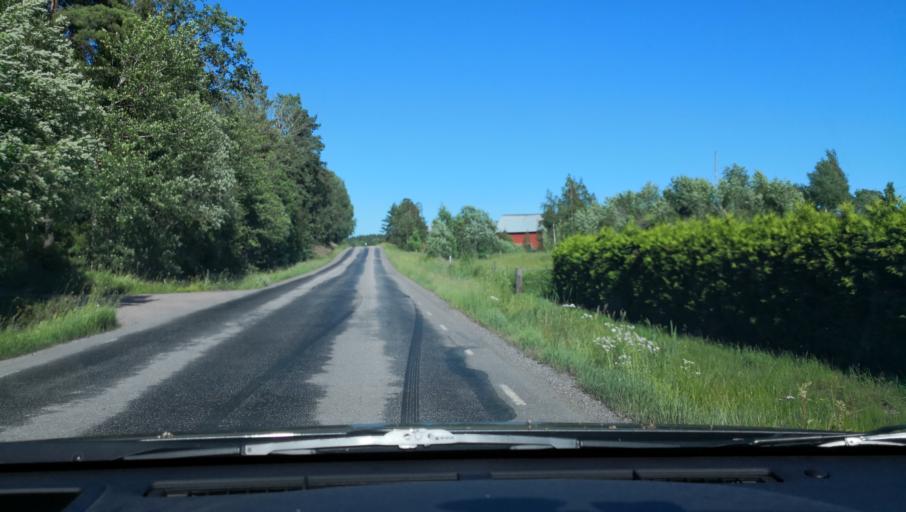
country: SE
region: Soedermanland
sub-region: Eskilstuna Kommun
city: Arla
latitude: 59.3254
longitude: 16.6530
